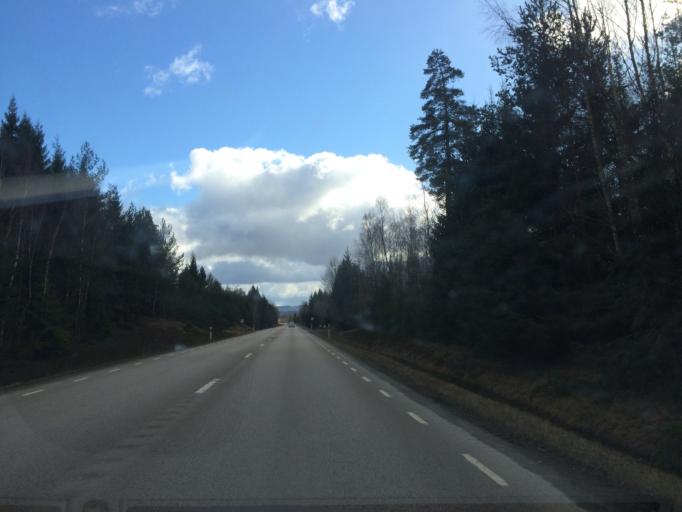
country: SE
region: Vaestra Goetaland
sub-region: Skara Kommun
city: Skara
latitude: 58.3032
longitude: 13.4680
